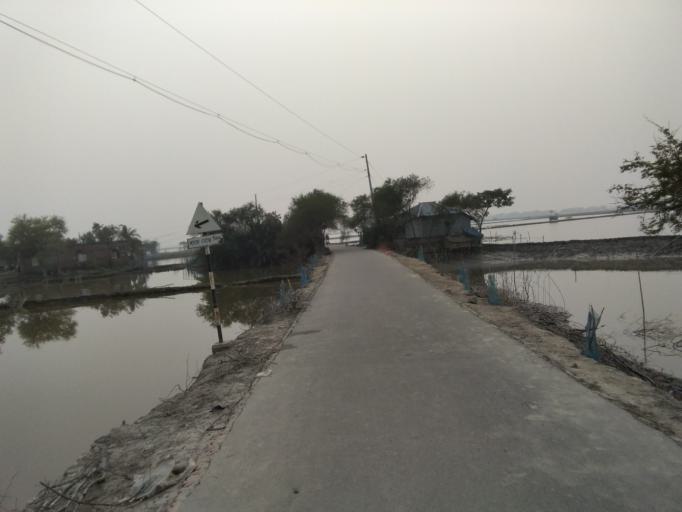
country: IN
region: West Bengal
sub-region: North 24 Parganas
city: Taki
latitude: 22.5826
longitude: 89.0568
